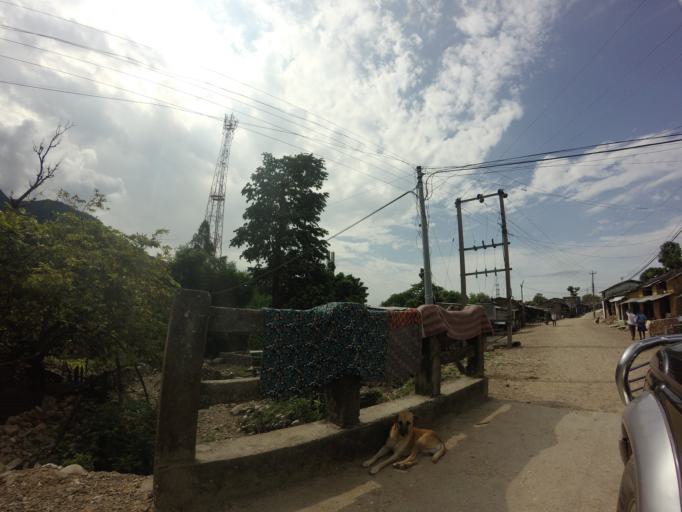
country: NP
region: Far Western
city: Tikapur
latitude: 28.6449
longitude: 81.2834
